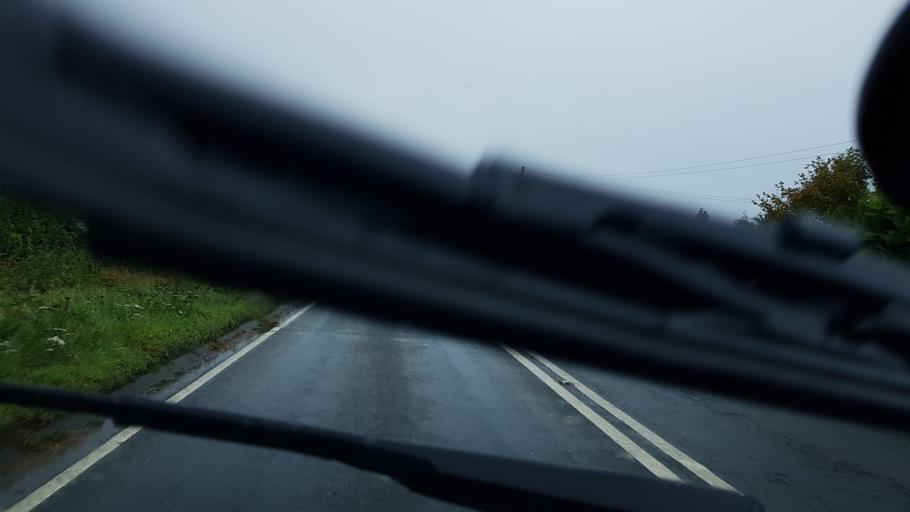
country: GB
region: England
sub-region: Worcestershire
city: Upton upon Severn
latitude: 52.0523
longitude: -2.1852
